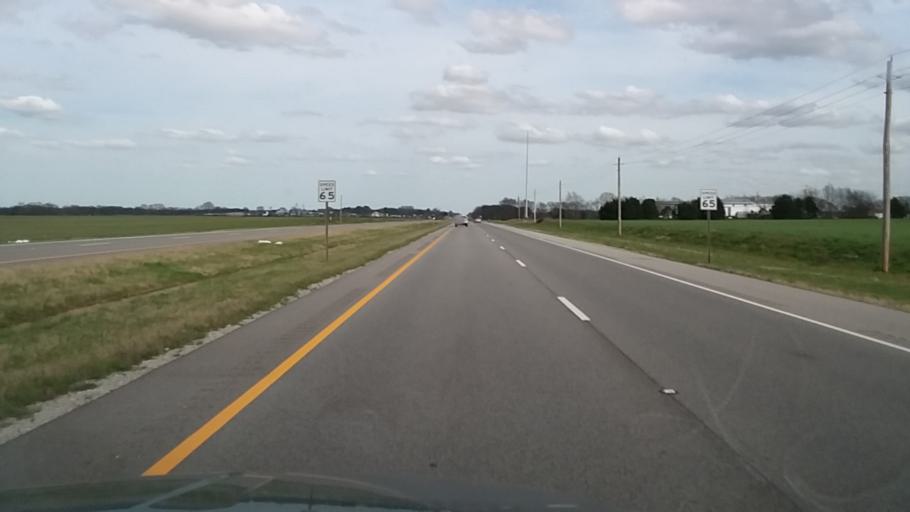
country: US
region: Alabama
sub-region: Colbert County
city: Muscle Shoals
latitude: 34.6852
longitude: -87.5884
